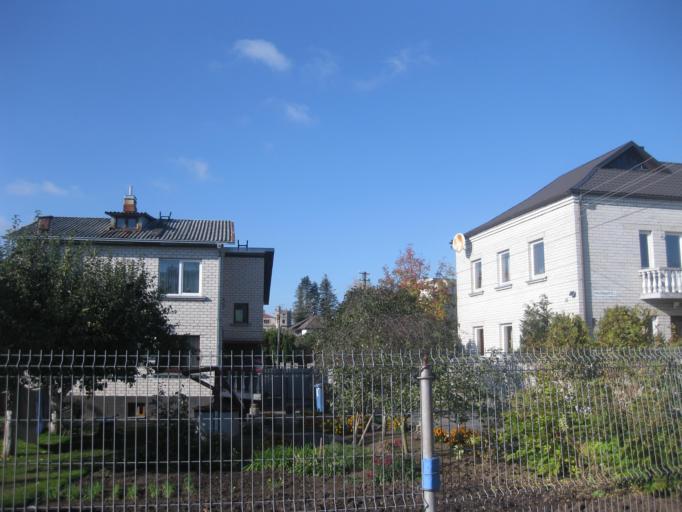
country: LT
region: Kauno apskritis
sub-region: Kauno rajonas
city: Garliava
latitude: 54.8338
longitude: 23.8683
